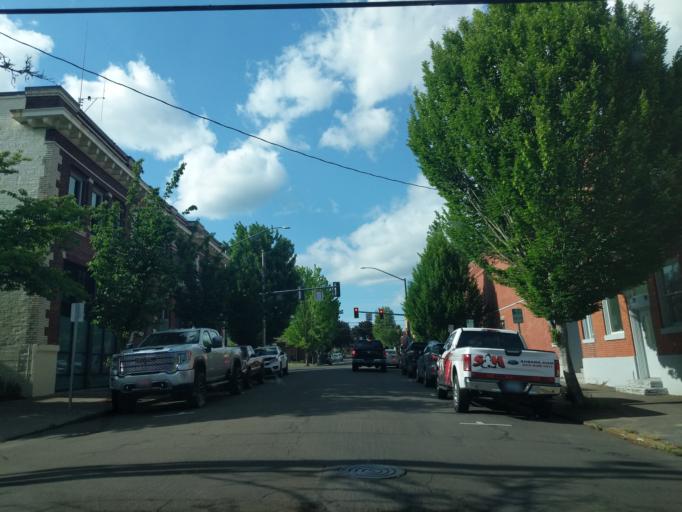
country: US
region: Oregon
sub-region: Yamhill County
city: Newberg
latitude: 45.2998
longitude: -122.9751
